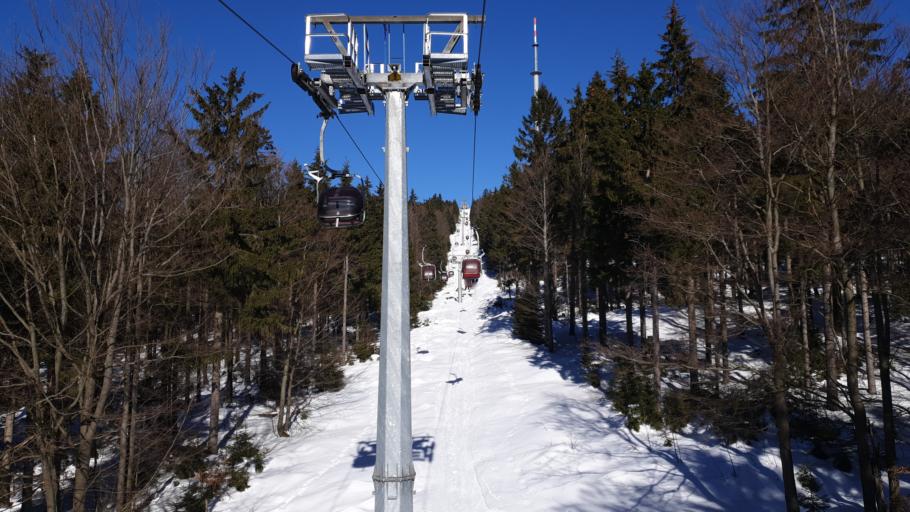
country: DE
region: Bavaria
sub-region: Upper Franconia
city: Bischofsgrun
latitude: 50.0239
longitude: 11.8080
